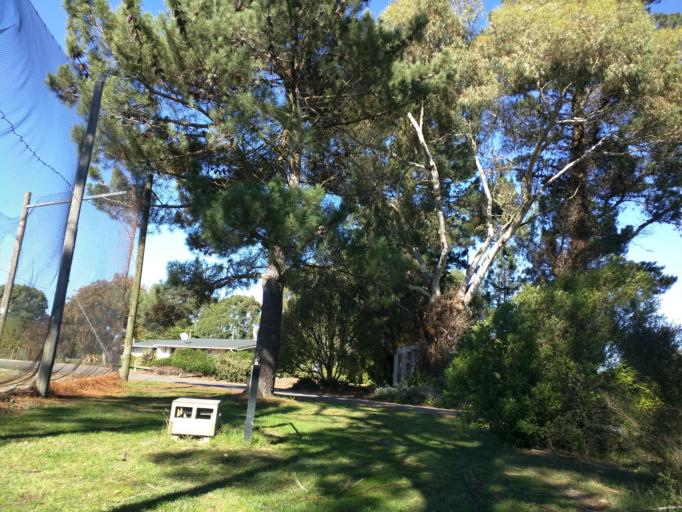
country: NZ
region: Canterbury
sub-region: Selwyn District
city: Lincoln
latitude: -43.6456
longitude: 172.4598
